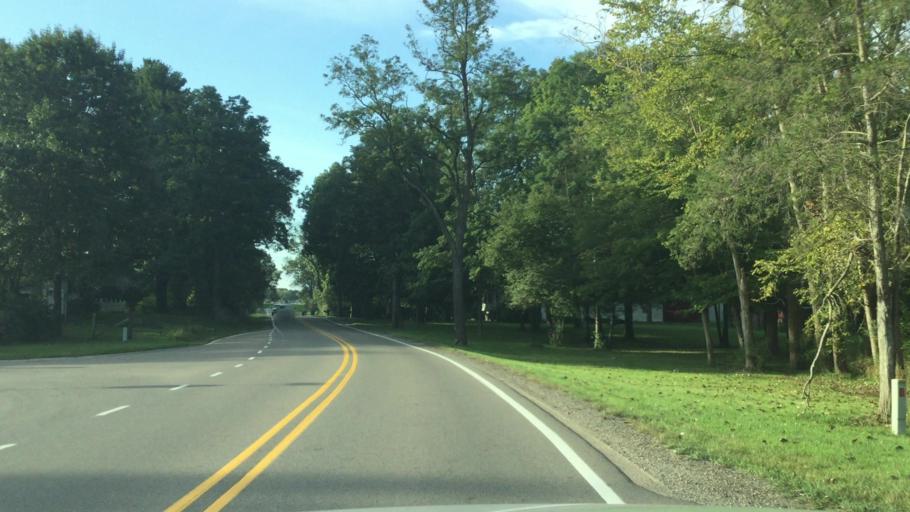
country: US
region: Michigan
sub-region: Livingston County
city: Whitmore Lake
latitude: 42.4608
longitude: -83.7991
